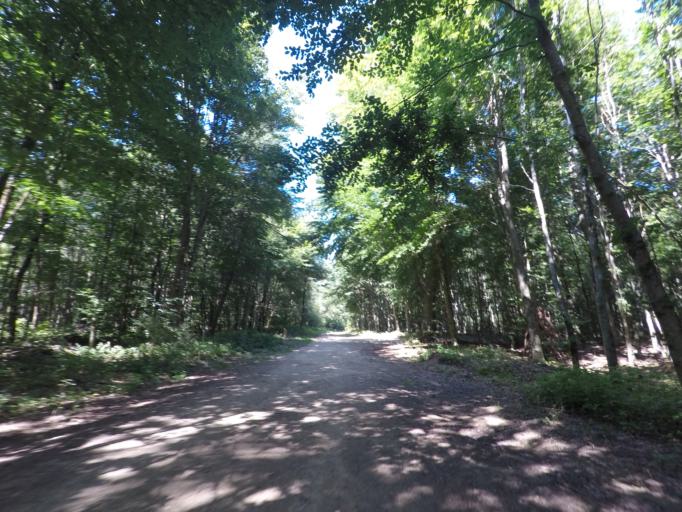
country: LU
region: Luxembourg
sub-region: Canton de Luxembourg
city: Luxembourg
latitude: 49.6330
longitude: 6.1131
